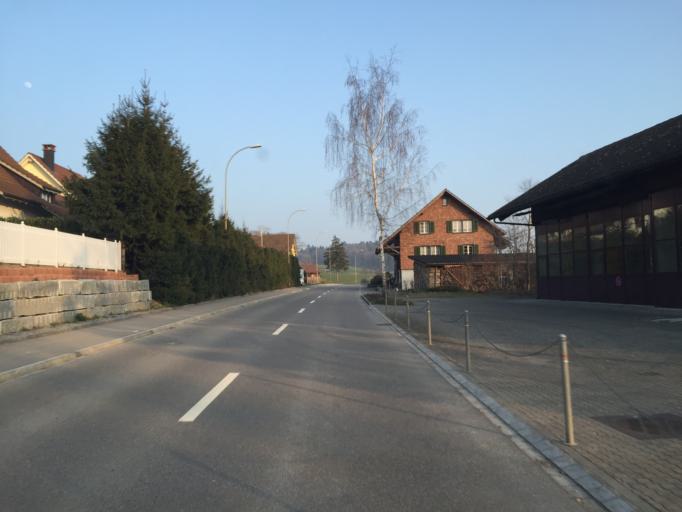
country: CH
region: Zurich
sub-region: Bezirk Andelfingen
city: Marthalen
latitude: 47.6518
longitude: 8.6569
